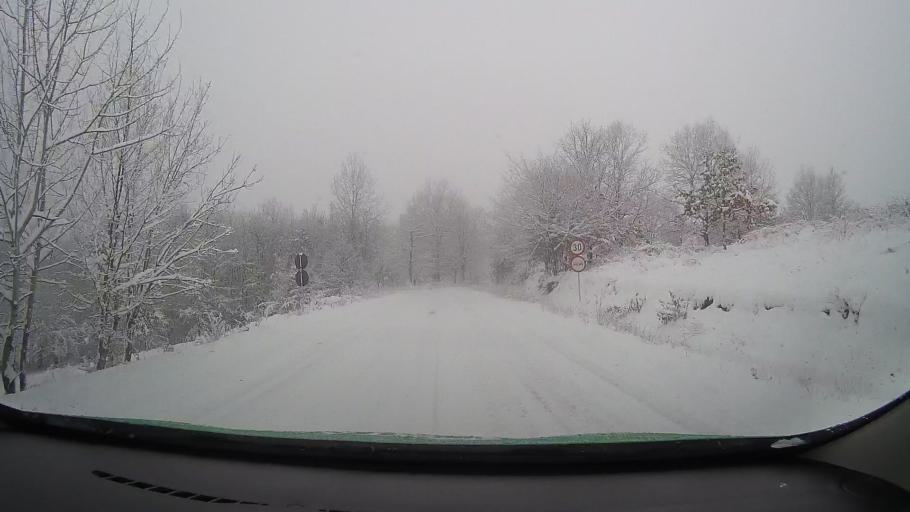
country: RO
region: Hunedoara
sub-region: Comuna Teliucu Inferior
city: Teliucu Inferior
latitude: 45.6921
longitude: 22.8929
